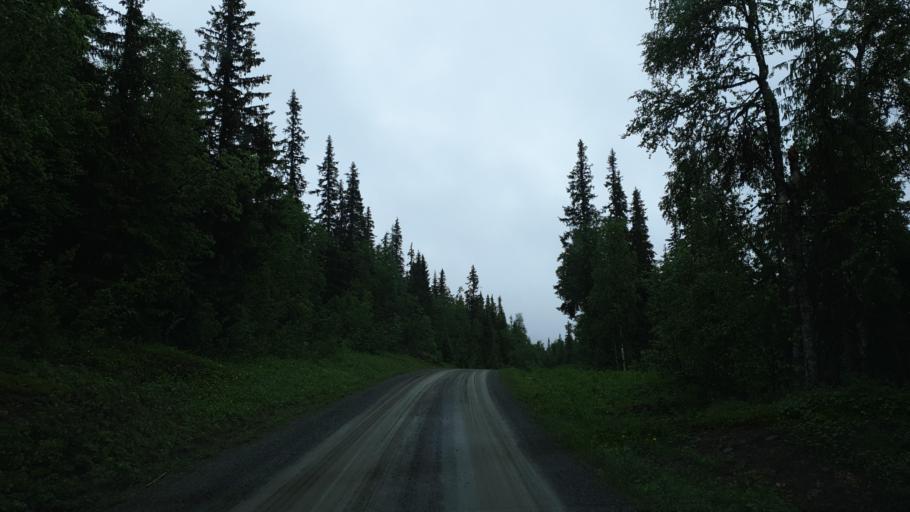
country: SE
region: Vaesterbotten
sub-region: Vilhelmina Kommun
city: Sjoberg
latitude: 65.3288
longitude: 15.9157
